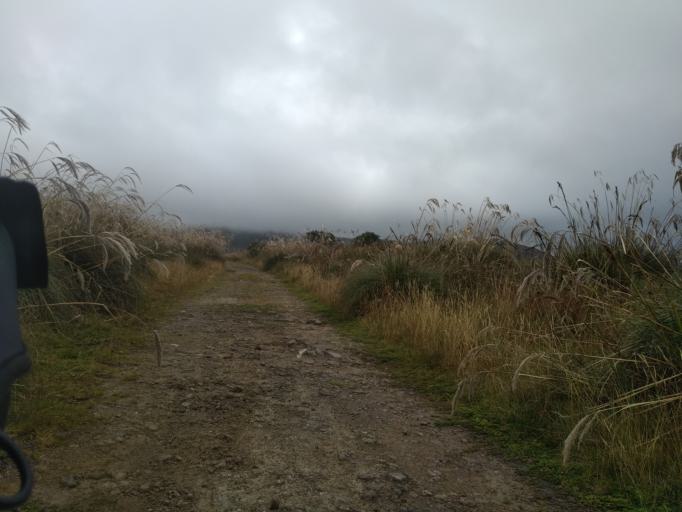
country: EC
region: Carchi
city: San Gabriel
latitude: 0.7099
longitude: -77.8220
